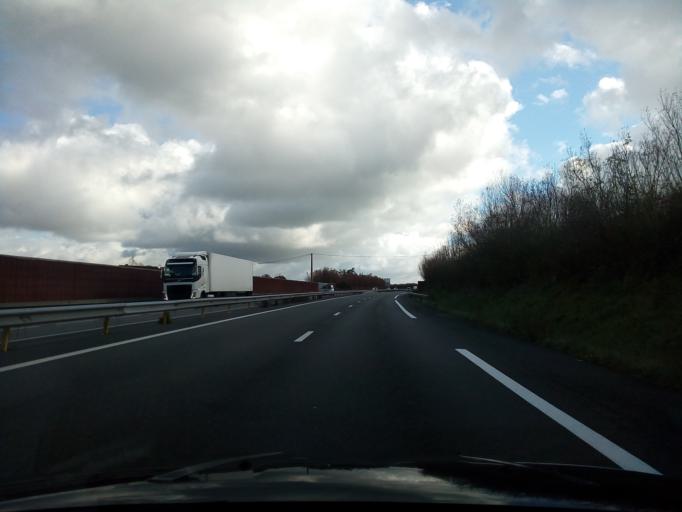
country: FR
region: Limousin
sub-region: Departement de la Creuse
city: Gouzon
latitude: 46.1991
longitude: 2.2446
